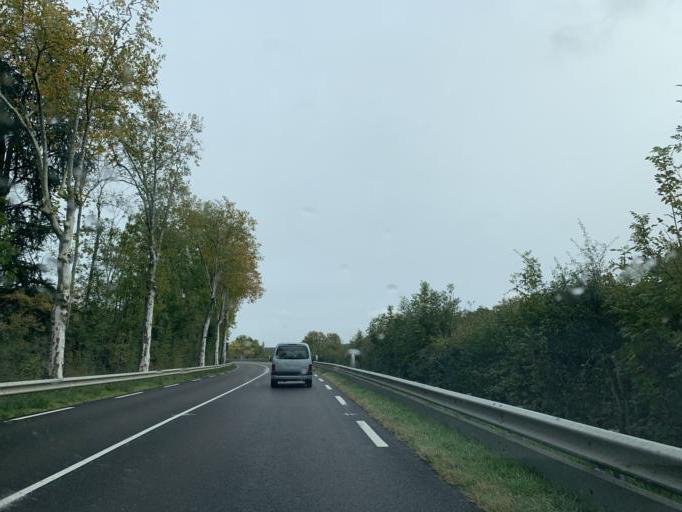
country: FR
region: Bourgogne
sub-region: Departement de l'Yonne
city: Venoy
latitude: 47.8543
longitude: 3.6448
